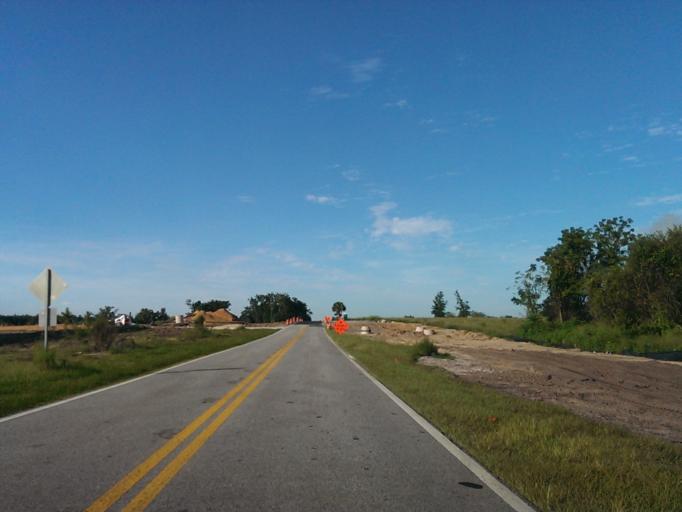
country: US
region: Florida
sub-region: Polk County
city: Citrus Ridge
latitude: 28.4294
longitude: -81.6163
